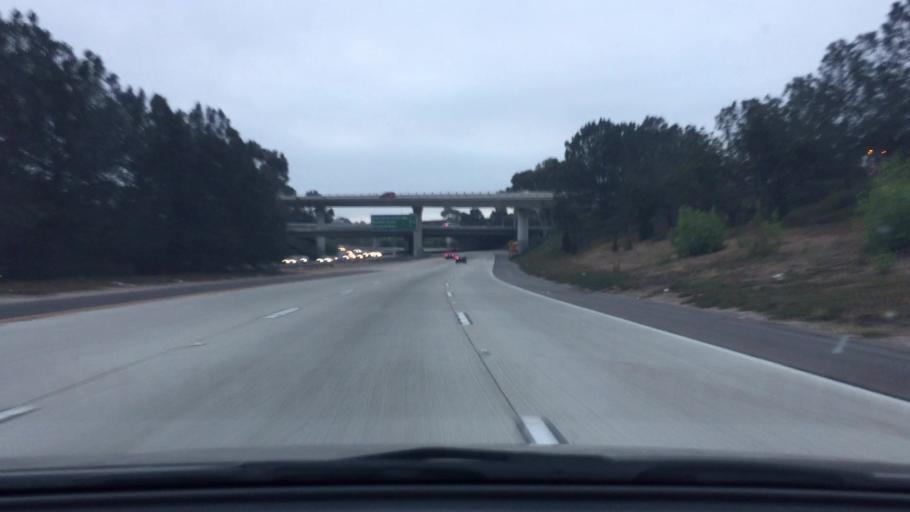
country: US
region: California
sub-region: San Diego County
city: Chula Vista
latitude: 32.6583
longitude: -117.0781
